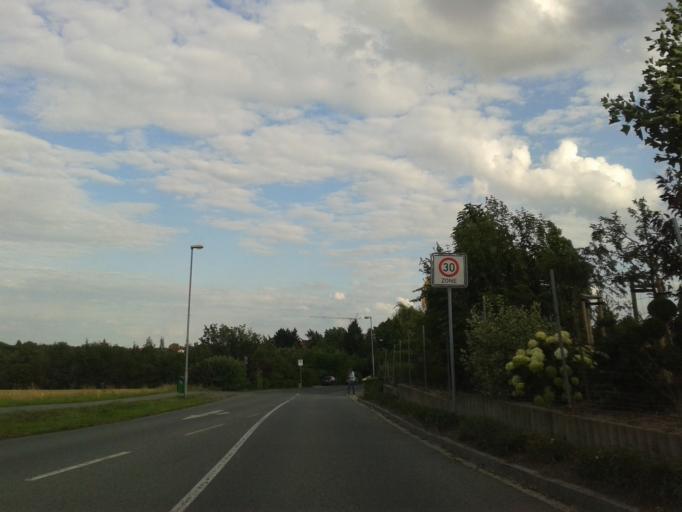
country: DE
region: Saxony
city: Bannewitz
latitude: 50.9977
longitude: 13.7197
